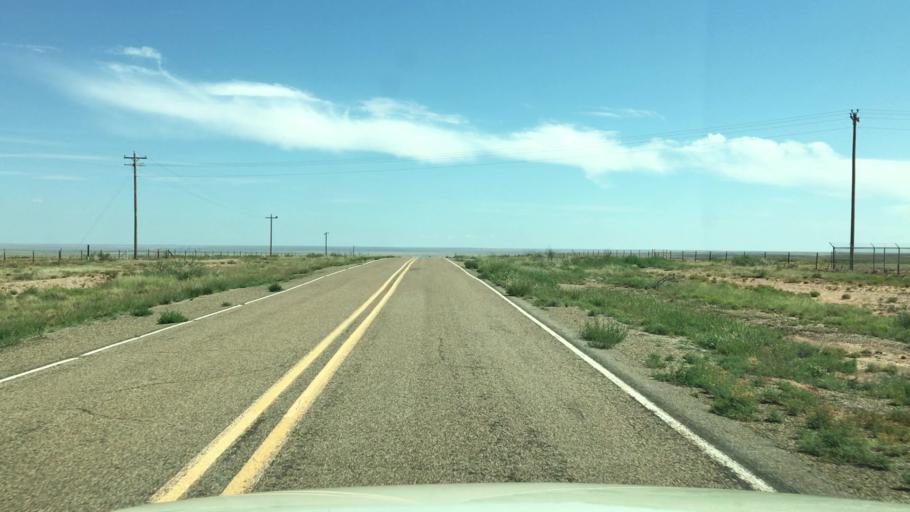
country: US
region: New Mexico
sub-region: Chaves County
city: Roswell
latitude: 33.9656
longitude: -104.5816
